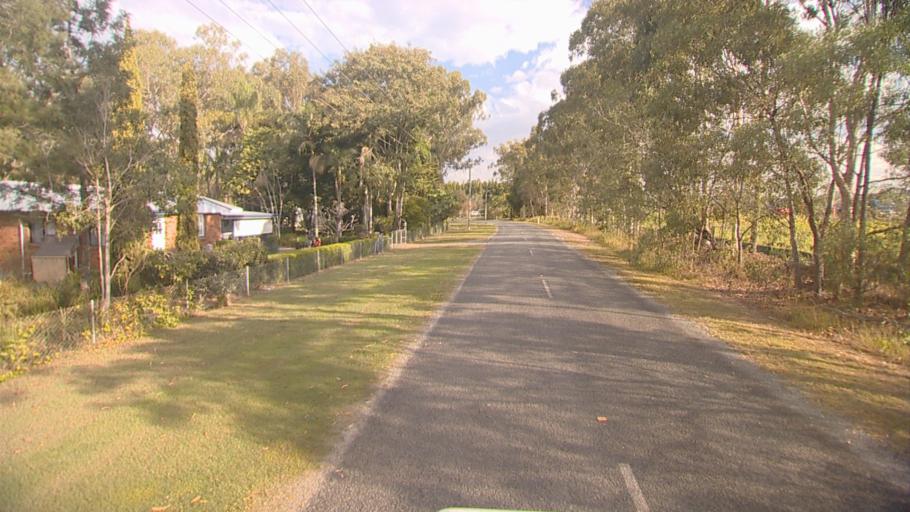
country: AU
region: Queensland
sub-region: Logan
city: Chambers Flat
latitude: -27.7759
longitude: 153.1038
